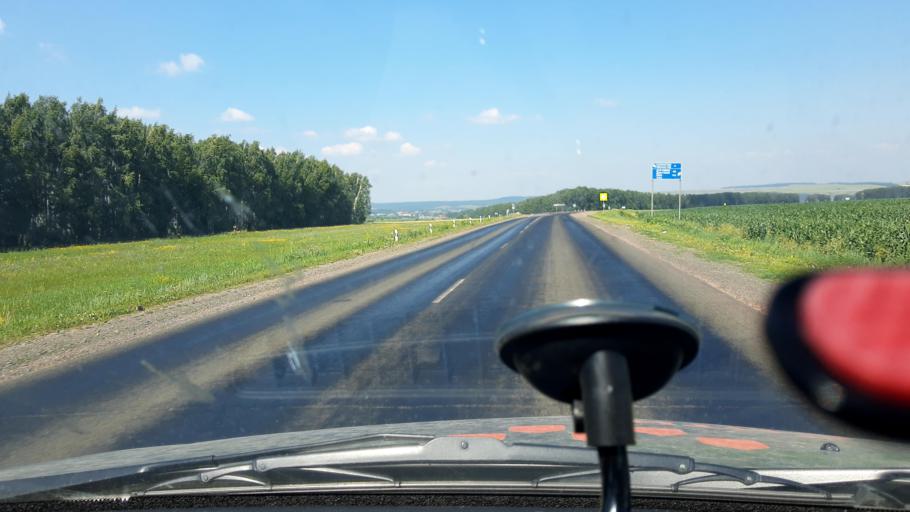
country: RU
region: Bashkortostan
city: Chekmagush
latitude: 55.1063
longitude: 54.6501
